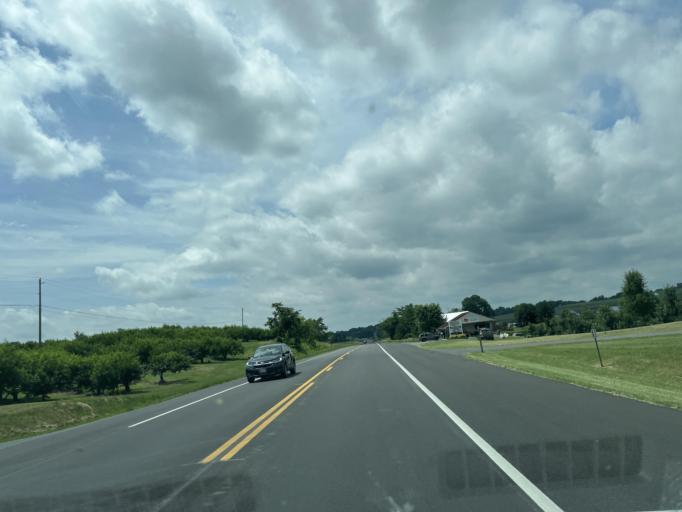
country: US
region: Pennsylvania
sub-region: Franklin County
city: Wayne Heights
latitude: 39.7172
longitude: -77.5472
